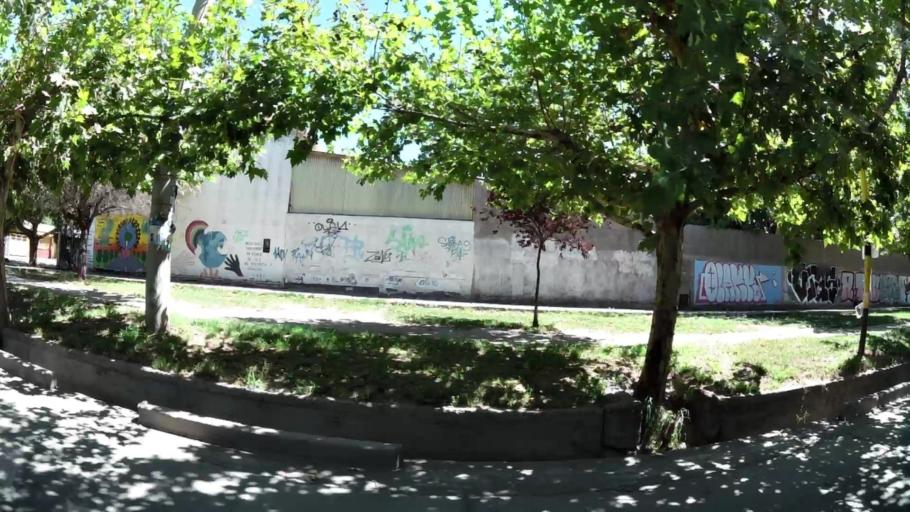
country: AR
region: Mendoza
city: Las Heras
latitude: -32.8481
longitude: -68.8468
